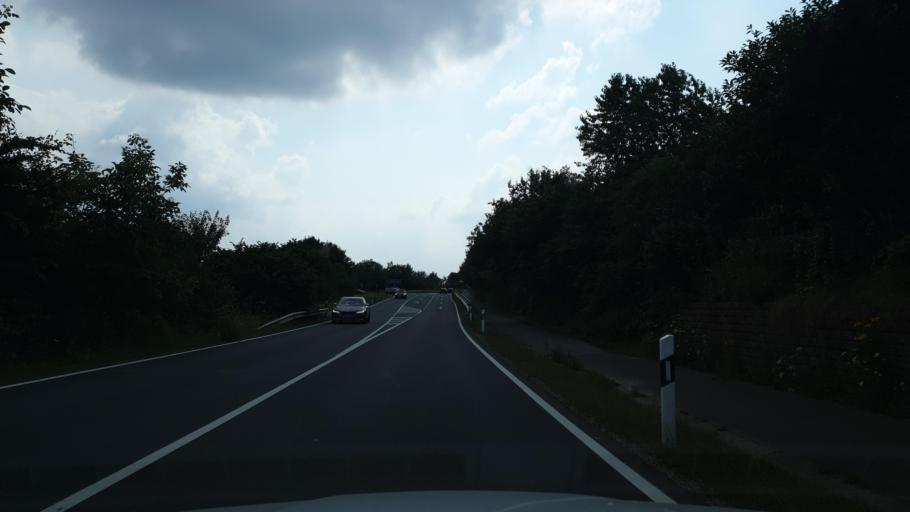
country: DE
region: North Rhine-Westphalia
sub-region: Regierungsbezirk Detmold
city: Bad Salzuflen
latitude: 52.1325
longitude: 8.7409
